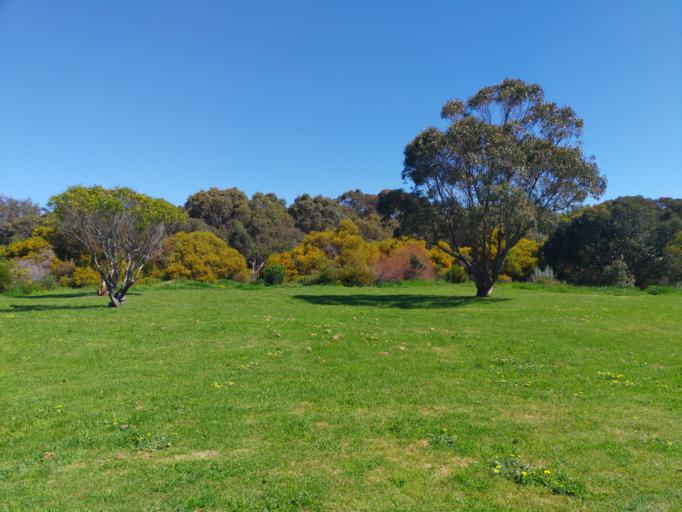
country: AU
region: Western Australia
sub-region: Bunbury
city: Bunbury
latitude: -33.3408
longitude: 115.6314
